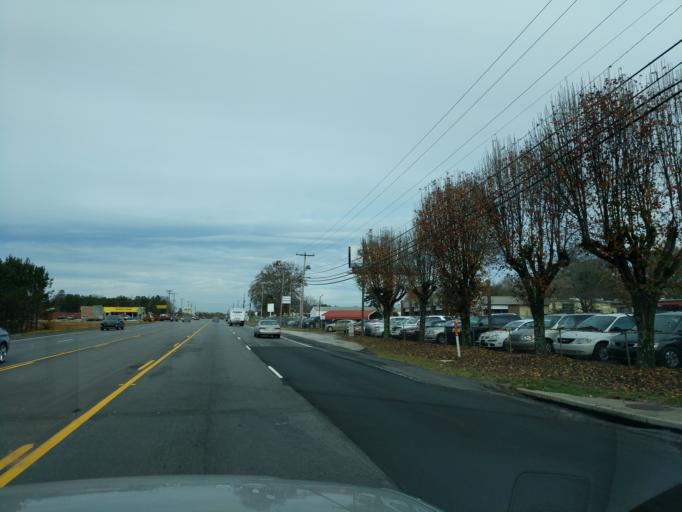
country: US
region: South Carolina
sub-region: Anderson County
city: Pendleton
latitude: 34.6249
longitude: -82.7789
